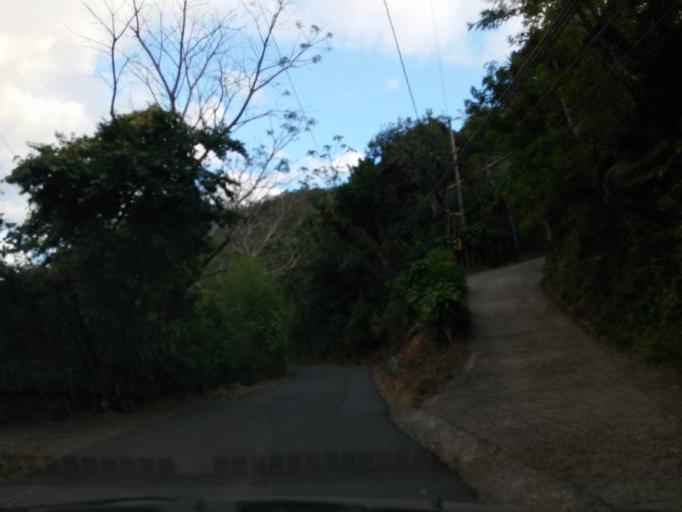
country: CR
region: San Jose
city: San Ignacio
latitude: 9.8071
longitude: -84.1760
